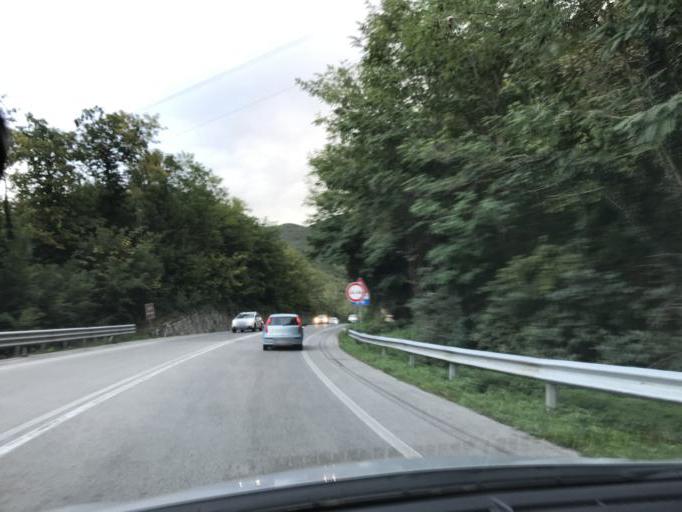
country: IT
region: Umbria
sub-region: Provincia di Terni
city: Ferentillo
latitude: 42.6675
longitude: 12.7290
